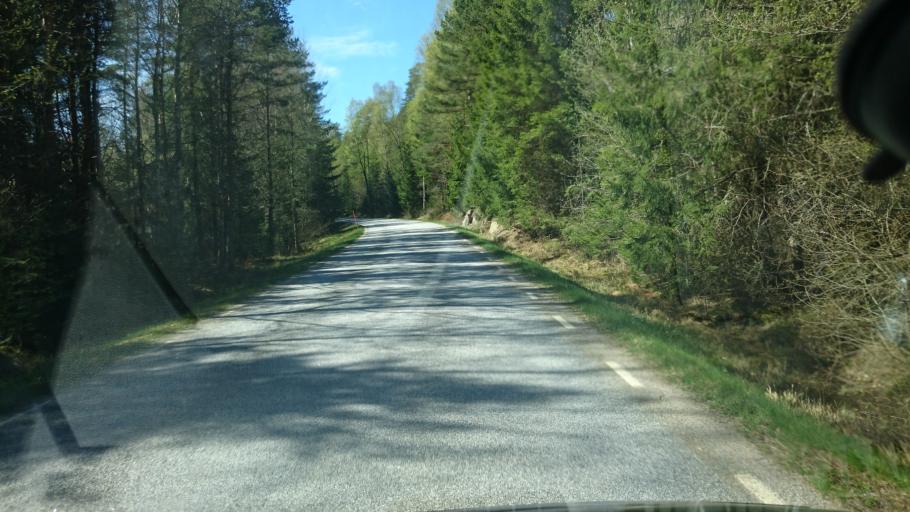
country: SE
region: Vaestra Goetaland
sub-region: Munkedals Kommun
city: Munkedal
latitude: 58.4067
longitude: 11.6677
